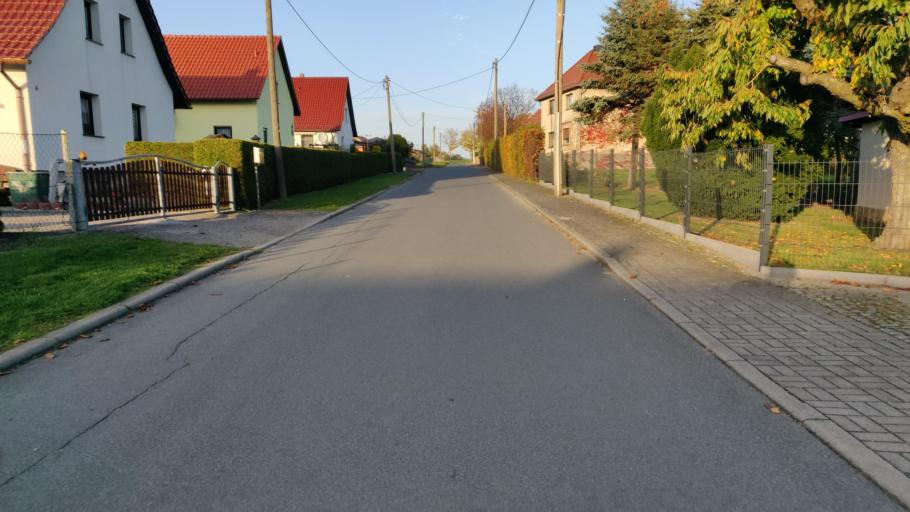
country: DE
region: Brandenburg
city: Grosskmehlen
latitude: 51.3532
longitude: 13.6949
